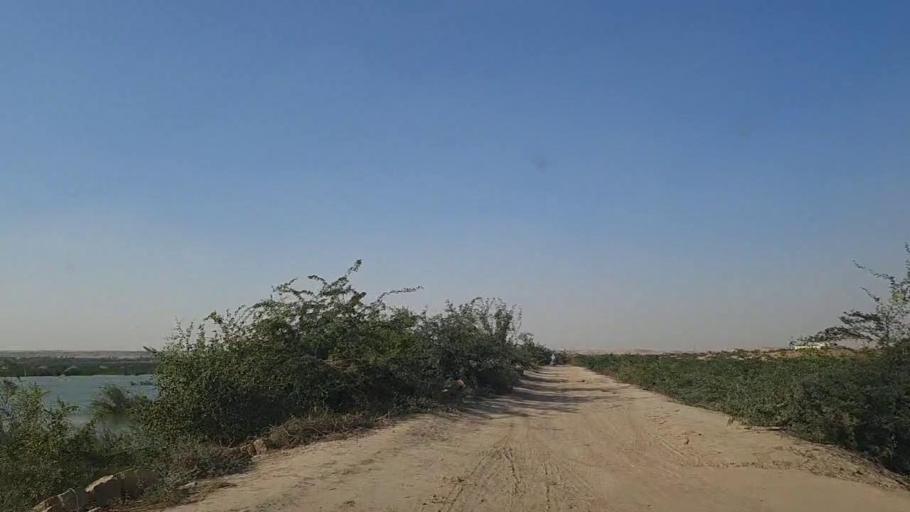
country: PK
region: Sindh
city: Daro Mehar
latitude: 25.0432
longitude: 68.1357
